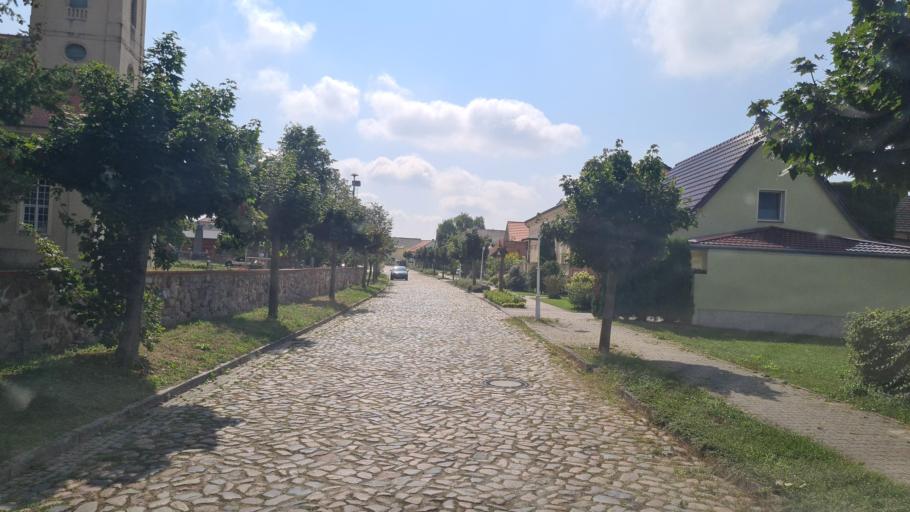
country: DE
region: Brandenburg
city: Trebbin
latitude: 52.2322
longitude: 13.3145
